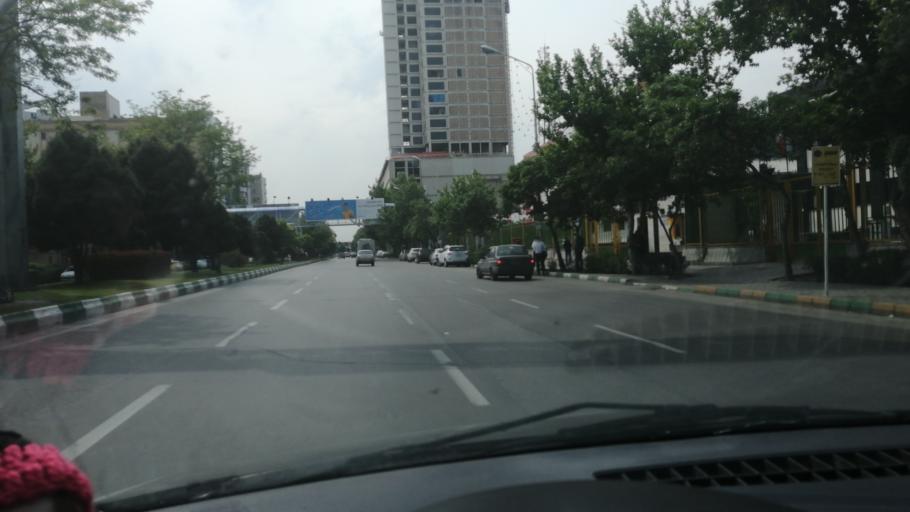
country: IR
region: Razavi Khorasan
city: Mashhad
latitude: 36.3243
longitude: 59.5681
